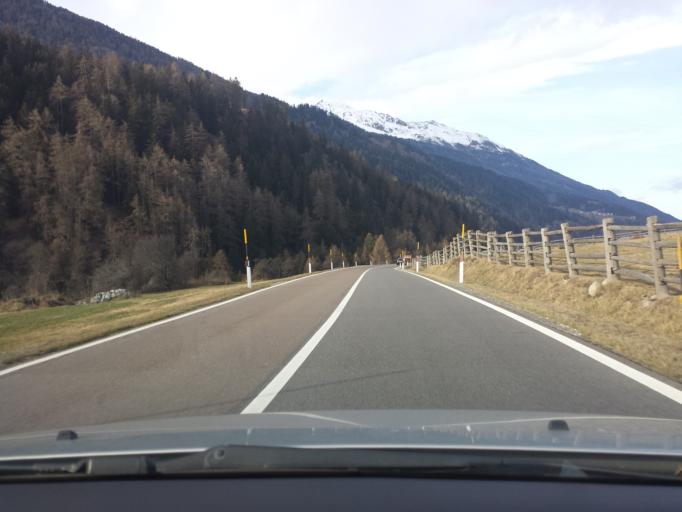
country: IT
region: Trentino-Alto Adige
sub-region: Bolzano
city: Malles Venosta
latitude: 46.7355
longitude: 10.5356
